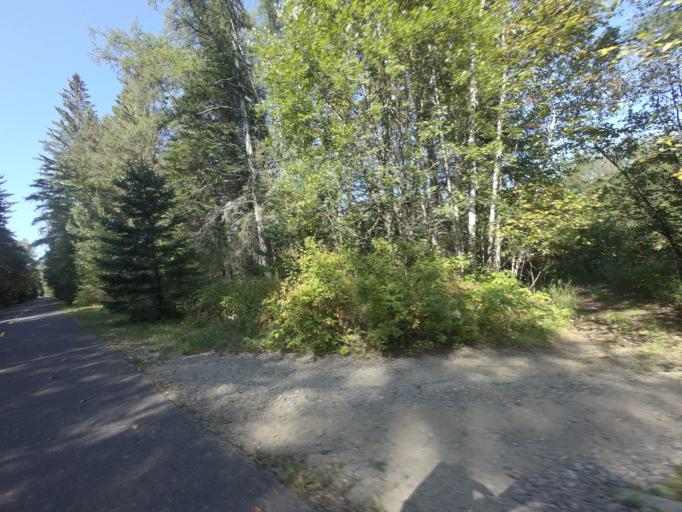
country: CA
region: Quebec
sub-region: Laurentides
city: Mont-Tremblant
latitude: 46.1259
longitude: -74.5458
